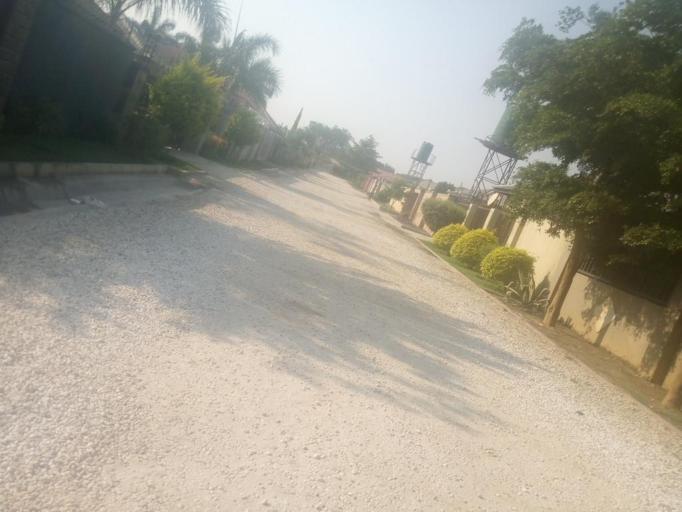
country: ZM
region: Lusaka
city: Lusaka
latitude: -15.3993
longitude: 28.3886
